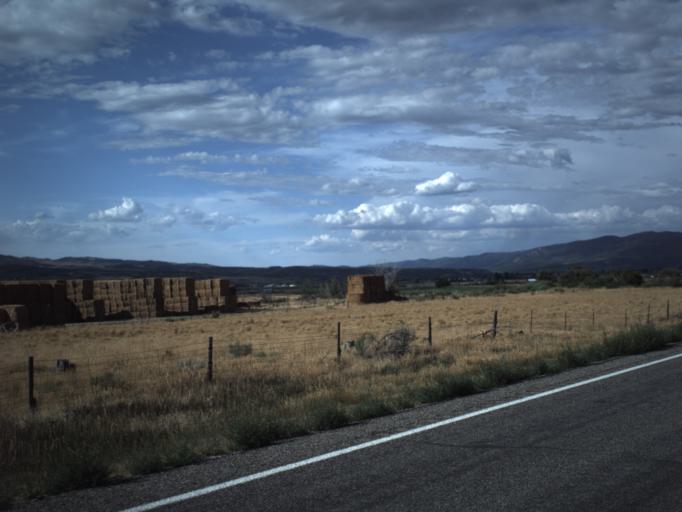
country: US
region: Utah
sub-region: Sanpete County
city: Mount Pleasant
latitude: 39.5133
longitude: -111.4928
